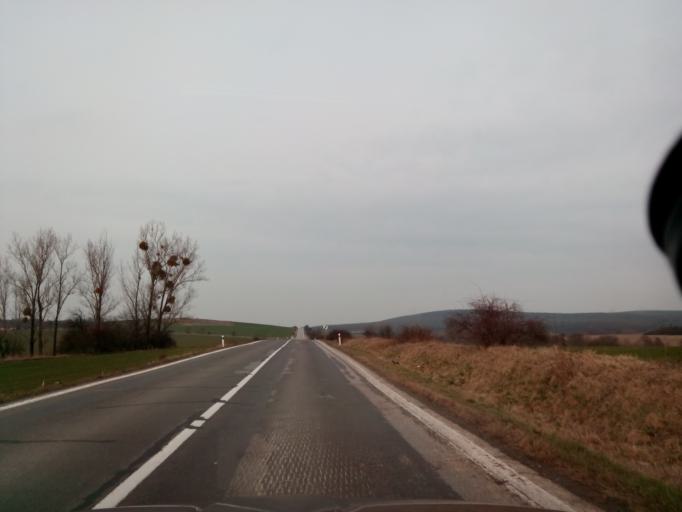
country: HU
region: Borsod-Abauj-Zemplen
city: Satoraljaujhely
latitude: 48.4780
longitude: 21.6430
